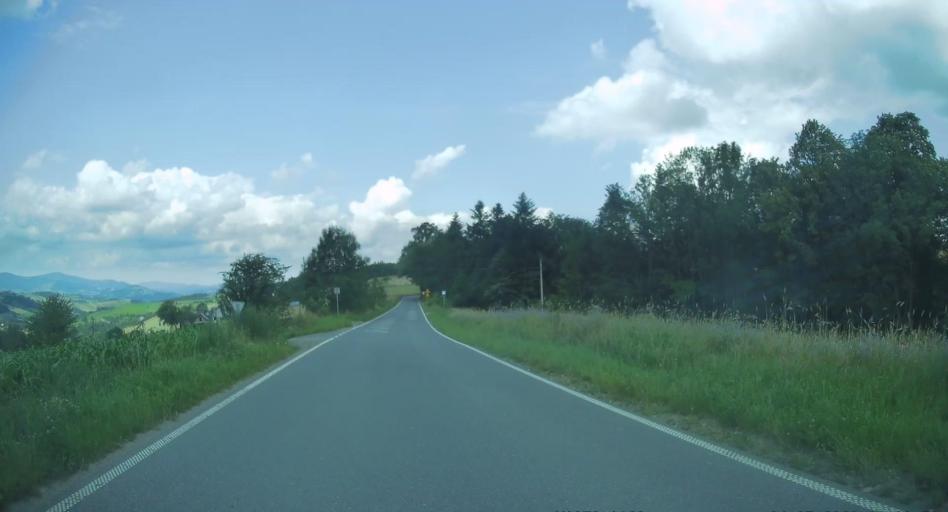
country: PL
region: Lesser Poland Voivodeship
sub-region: Powiat nowosadecki
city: Korzenna
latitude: 49.6980
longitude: 20.7628
